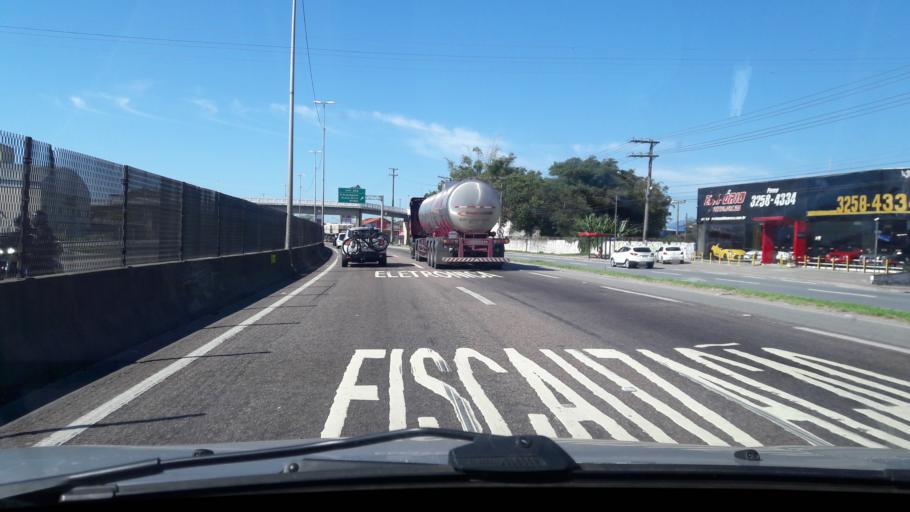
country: BR
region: Santa Catarina
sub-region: Sao Jose
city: Campinas
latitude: -27.5557
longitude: -48.6193
